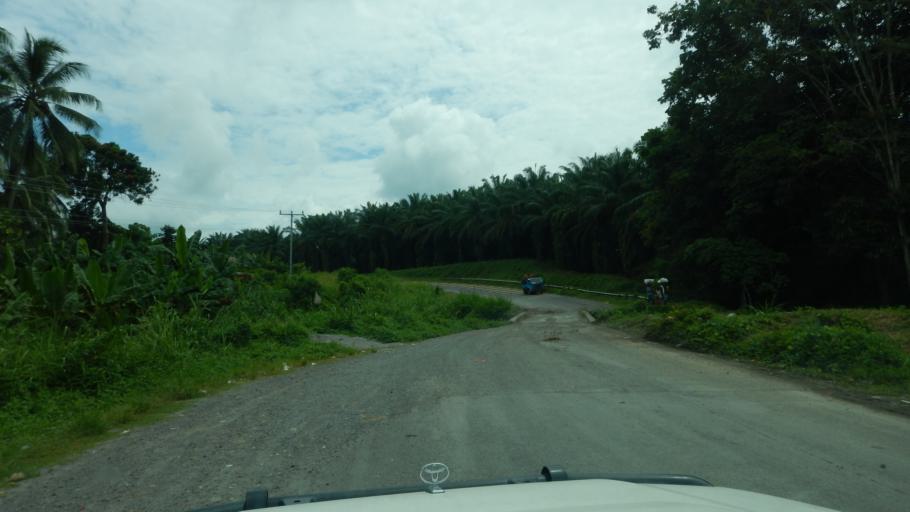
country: PG
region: Northern Province
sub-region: Sohe
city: Popondetta
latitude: -8.7668
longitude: 148.1761
